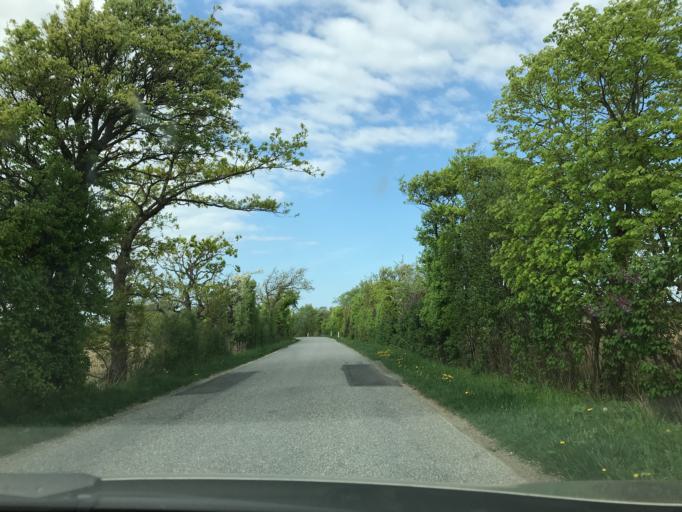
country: DK
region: South Denmark
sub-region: Middelfart Kommune
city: Norre Aby
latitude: 55.3916
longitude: 9.8560
